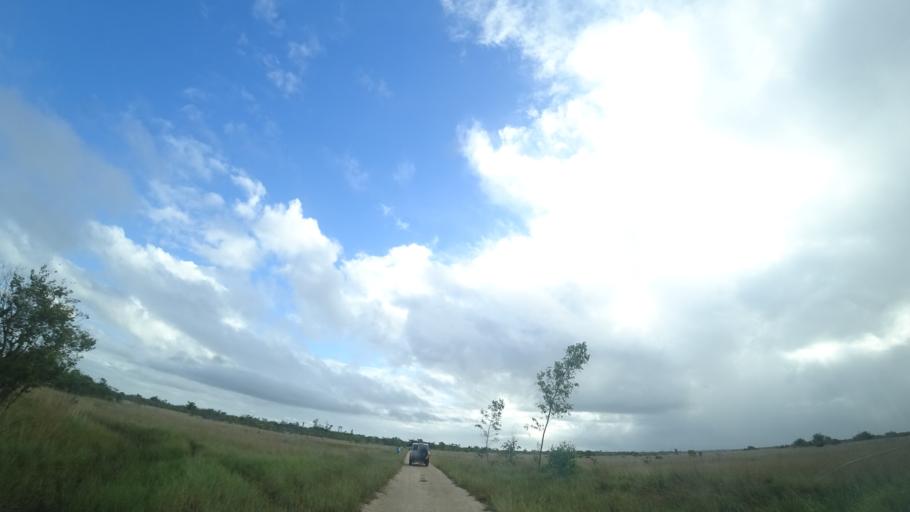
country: MZ
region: Sofala
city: Beira
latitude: -19.6469
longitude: 35.0588
